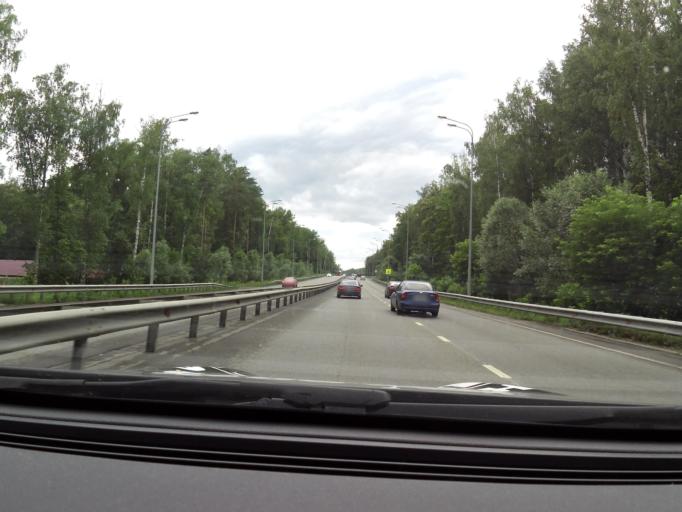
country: RU
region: Tatarstan
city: Staroye Arakchino
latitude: 55.8434
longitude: 48.9379
